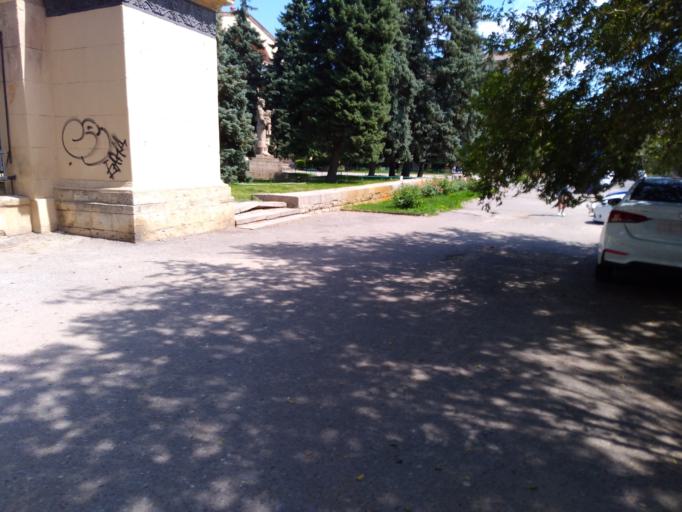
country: RU
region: Volgograd
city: Volgograd
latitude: 48.7144
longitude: 44.5235
